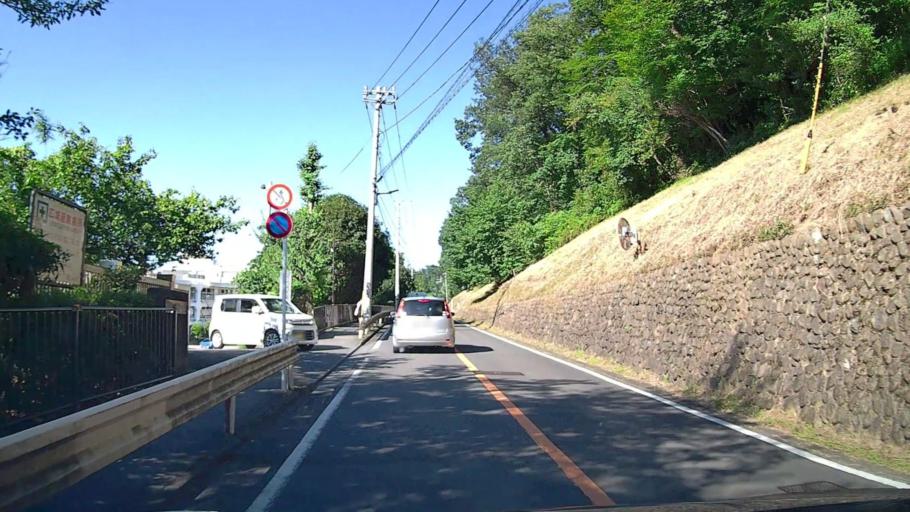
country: JP
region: Tokyo
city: Fussa
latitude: 35.7748
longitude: 139.3581
